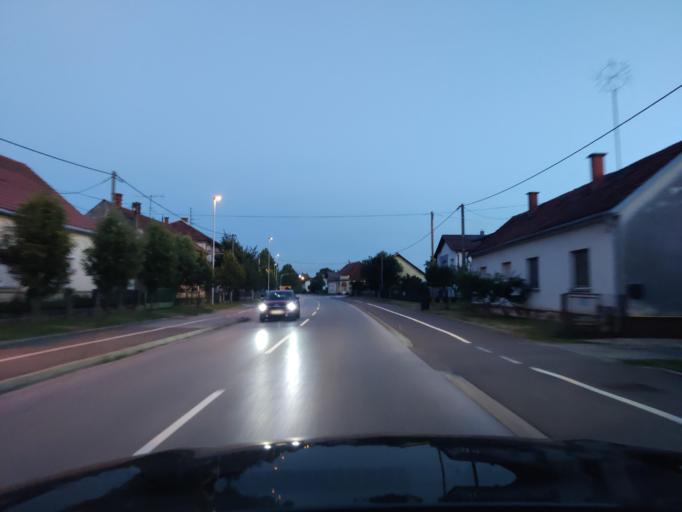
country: SI
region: Lendava-Lendva
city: Lendava
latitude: 46.5577
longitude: 16.4475
